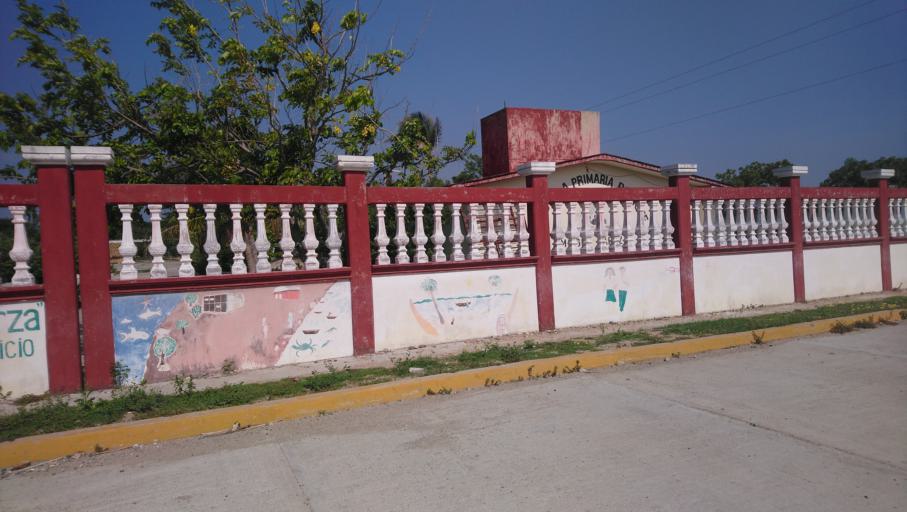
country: MX
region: Oaxaca
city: San Mateo del Mar
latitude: 16.2059
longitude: -94.9823
